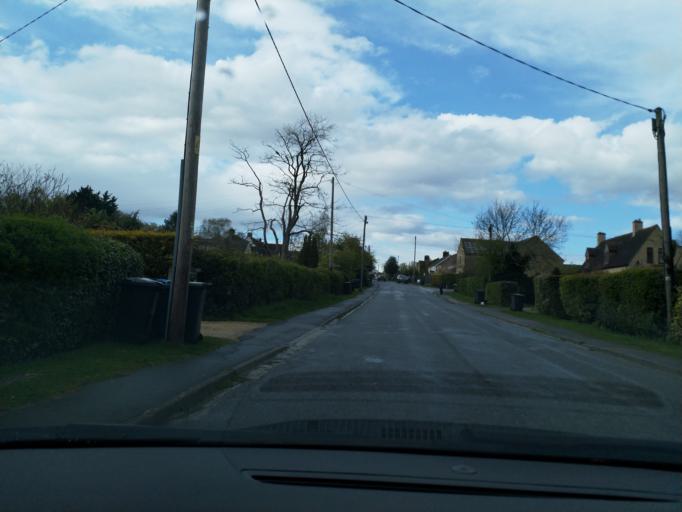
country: GB
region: England
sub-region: Oxfordshire
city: North Leigh
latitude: 51.8110
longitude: -1.4417
